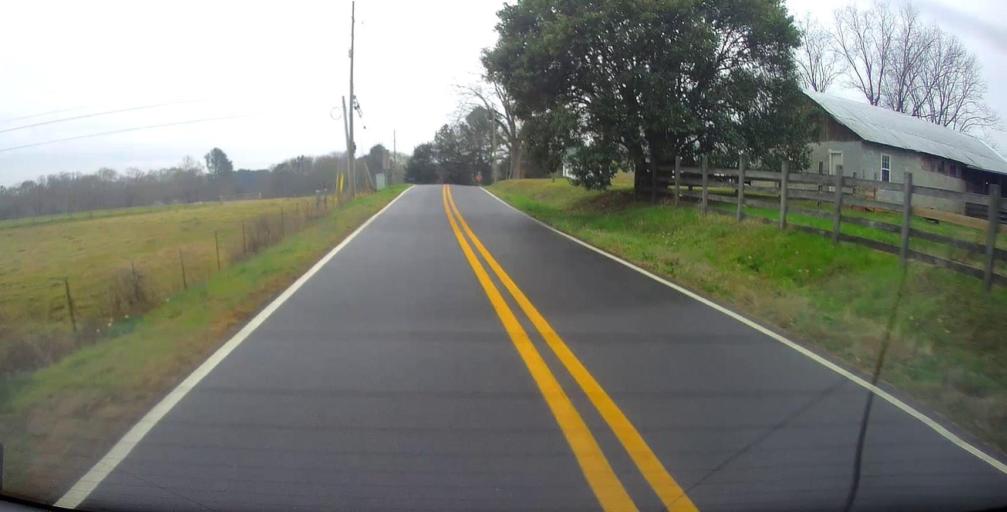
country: US
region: Georgia
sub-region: Monroe County
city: Forsyth
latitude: 33.0551
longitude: -83.8917
